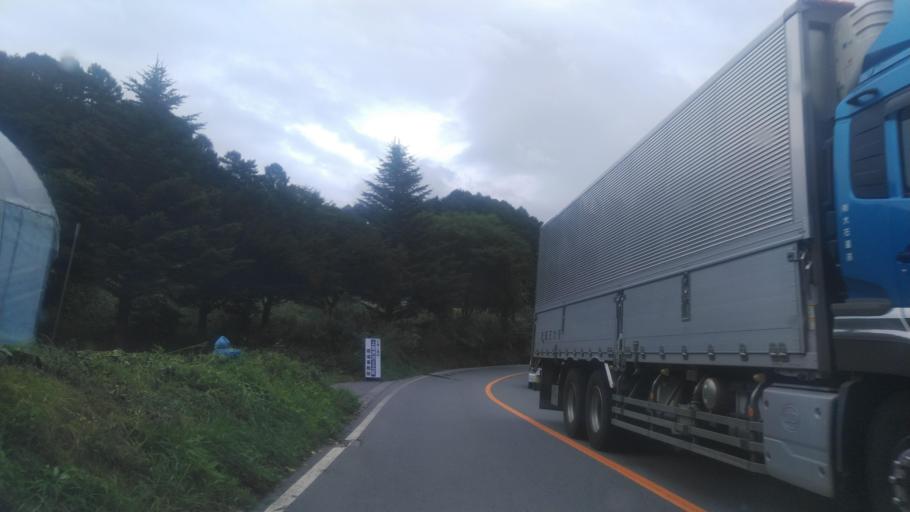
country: JP
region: Nagano
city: Ueda
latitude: 36.4887
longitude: 138.3729
